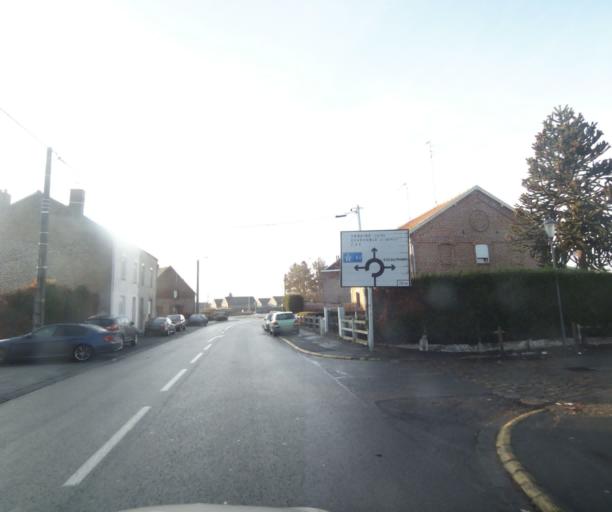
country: FR
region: Nord-Pas-de-Calais
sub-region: Departement du Nord
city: Vicq
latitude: 50.4058
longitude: 3.6030
